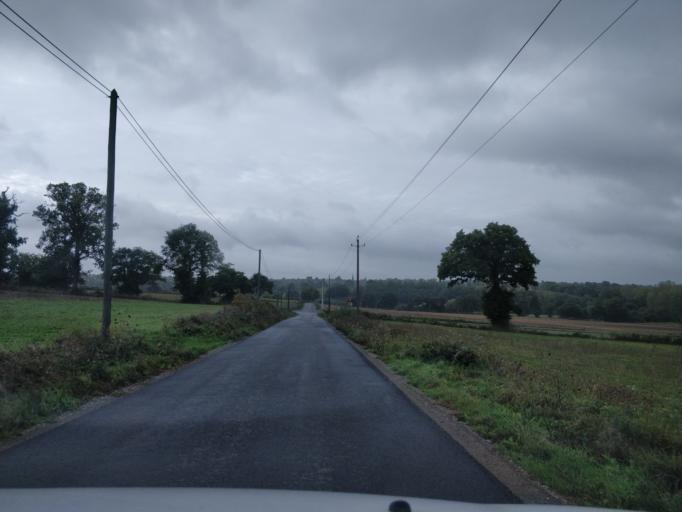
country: FR
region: Brittany
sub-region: Departement d'Ille-et-Vilaine
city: La Bouexiere
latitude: 48.1989
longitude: -1.4356
